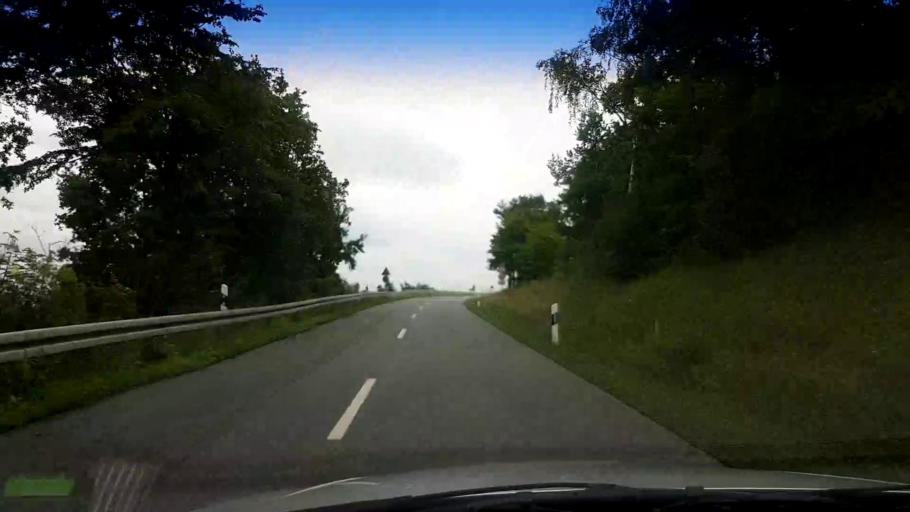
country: DE
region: Bavaria
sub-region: Upper Franconia
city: Mainleus
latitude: 50.0895
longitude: 11.3494
